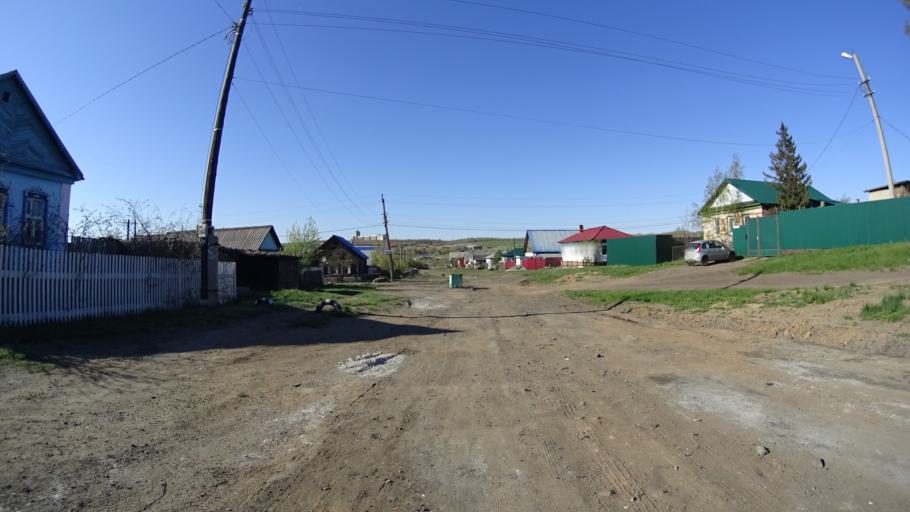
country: RU
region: Chelyabinsk
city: Troitsk
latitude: 54.0913
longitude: 61.5999
